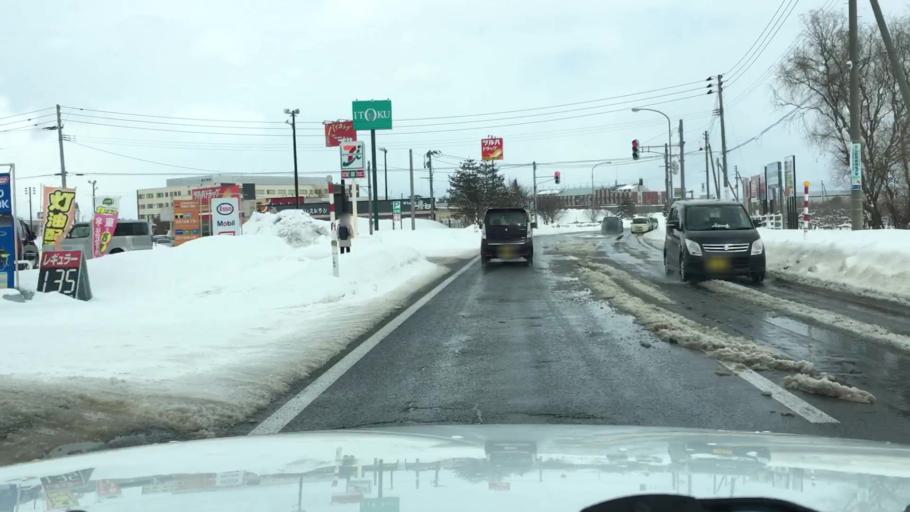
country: JP
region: Aomori
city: Hirosaki
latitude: 40.5838
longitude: 140.4993
